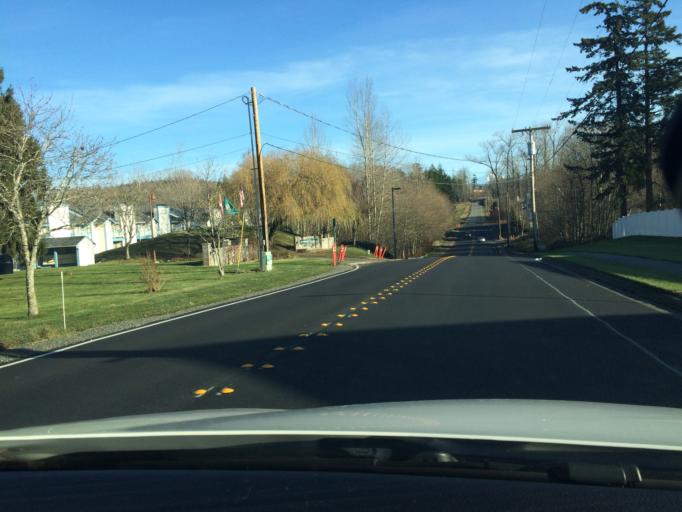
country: US
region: Washington
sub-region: Whatcom County
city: Bellingham
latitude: 48.7951
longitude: -122.4826
